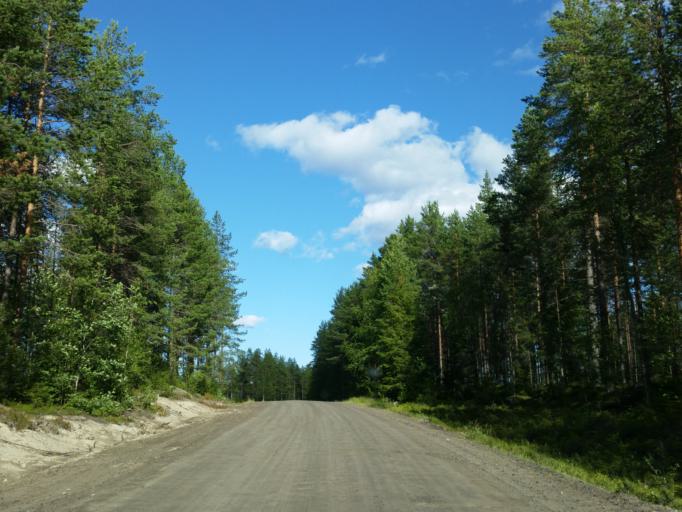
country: SE
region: Vaesterbotten
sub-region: Robertsfors Kommun
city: Robertsfors
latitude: 64.1385
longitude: 20.8745
